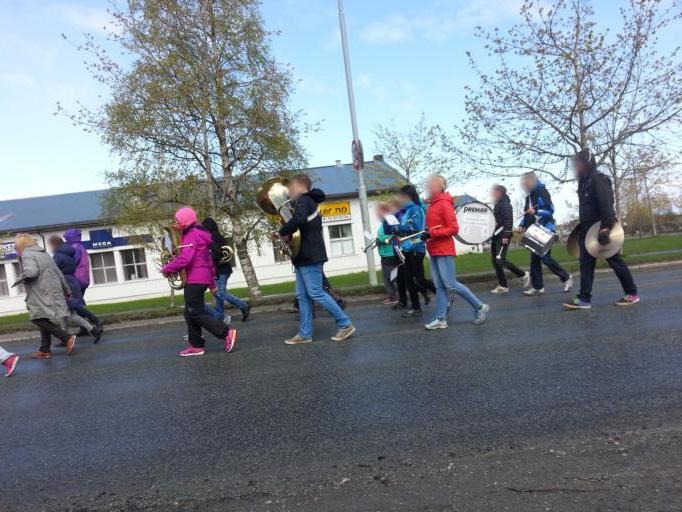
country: NO
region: Sor-Trondelag
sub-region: Trondheim
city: Trondheim
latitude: 63.3940
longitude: 10.3678
